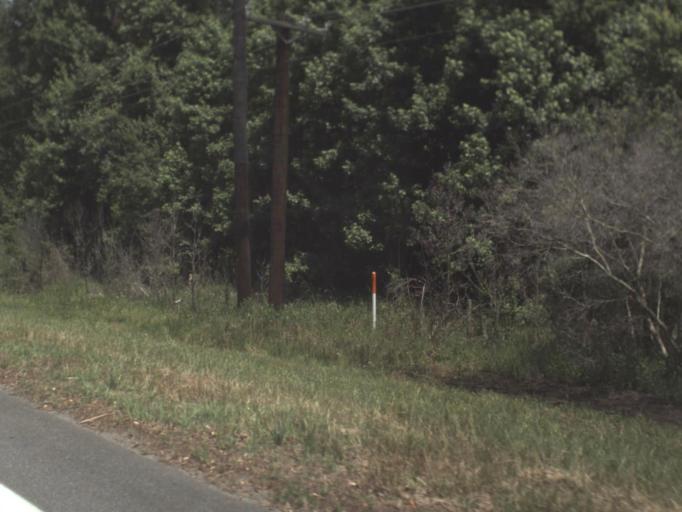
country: US
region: Florida
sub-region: Union County
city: Lake Butler
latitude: 30.0178
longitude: -82.3129
